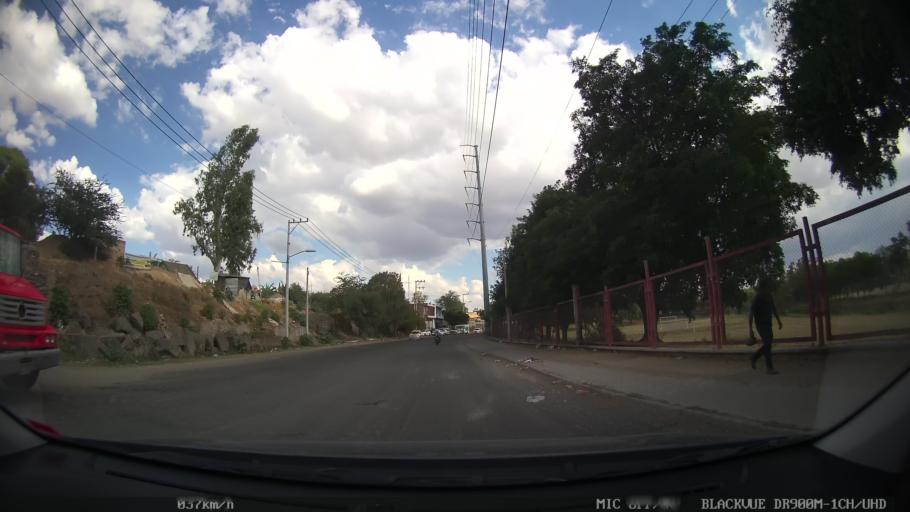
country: MX
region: Jalisco
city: Tlaquepaque
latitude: 20.6602
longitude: -103.2682
